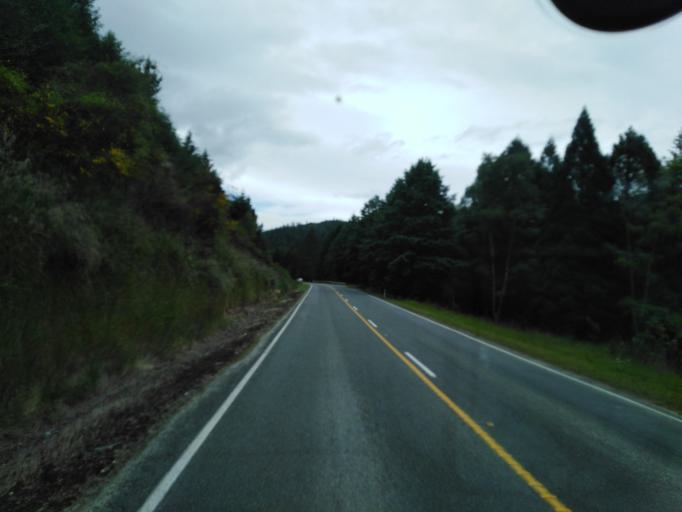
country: NZ
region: Tasman
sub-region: Tasman District
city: Wakefield
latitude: -41.4802
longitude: 172.8769
